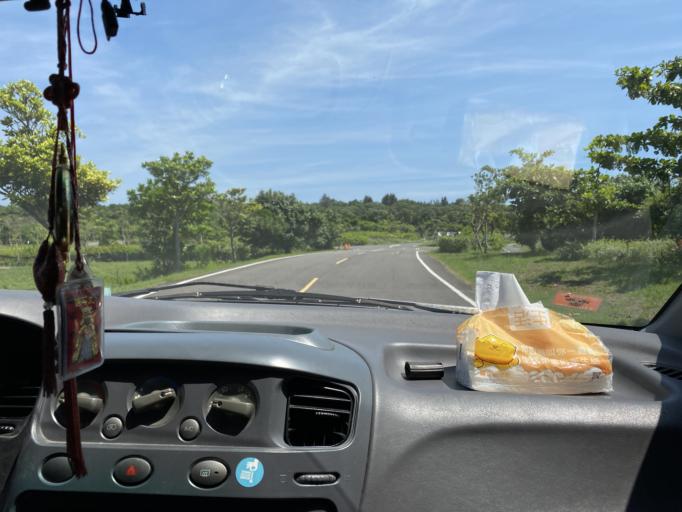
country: TW
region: Taiwan
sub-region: Yilan
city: Yilan
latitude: 24.7385
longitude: 121.8184
